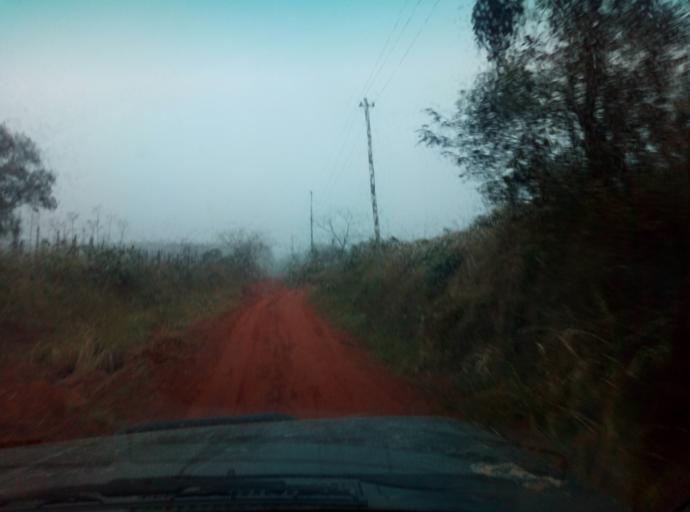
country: PY
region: Caaguazu
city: Doctor Cecilio Baez
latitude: -25.1604
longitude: -56.2618
